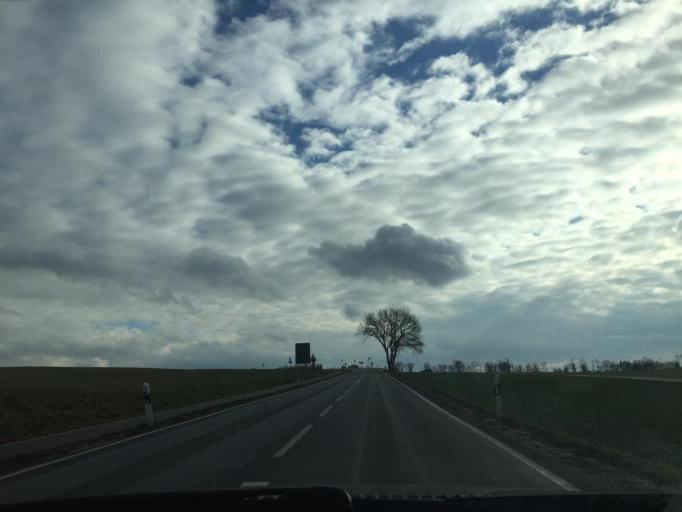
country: DE
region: Saxony
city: Ottendorf-Okrilla
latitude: 51.1694
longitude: 13.8601
